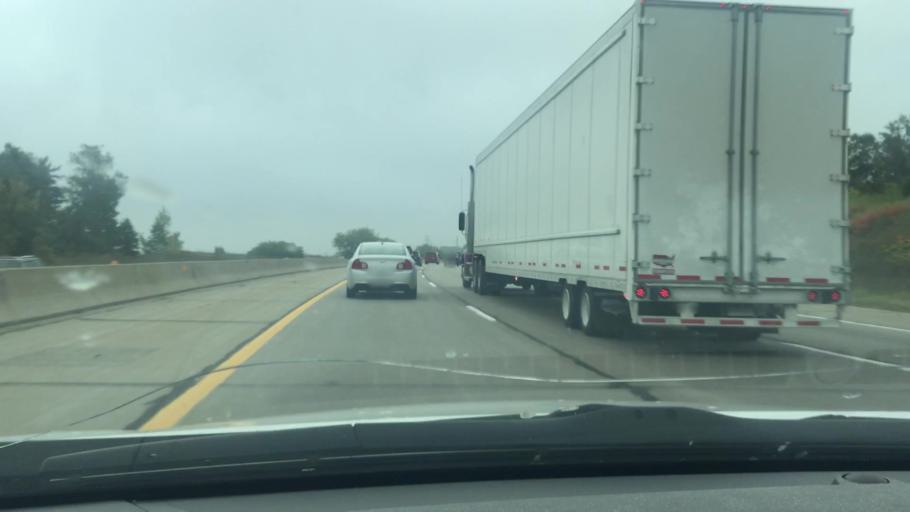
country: US
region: Michigan
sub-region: Livingston County
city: Howell
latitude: 42.5836
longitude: -83.9029
